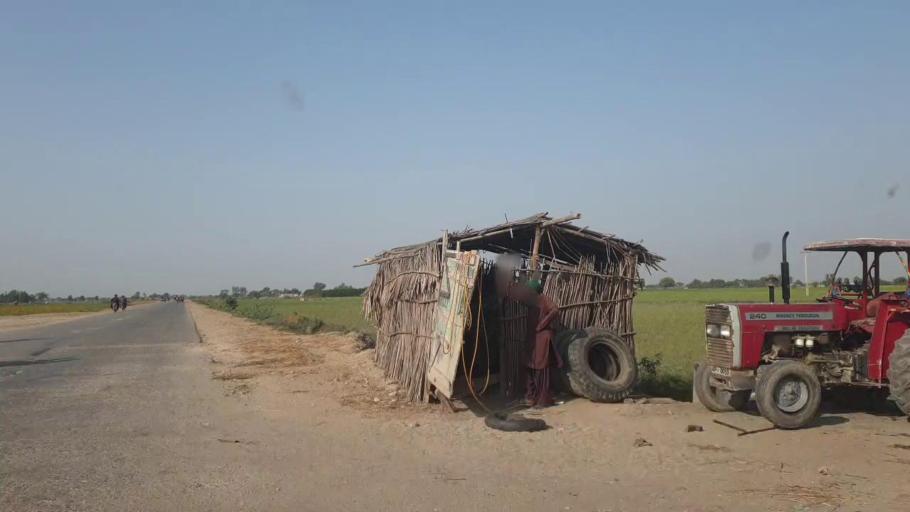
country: PK
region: Sindh
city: Kario
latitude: 24.5997
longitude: 68.5355
